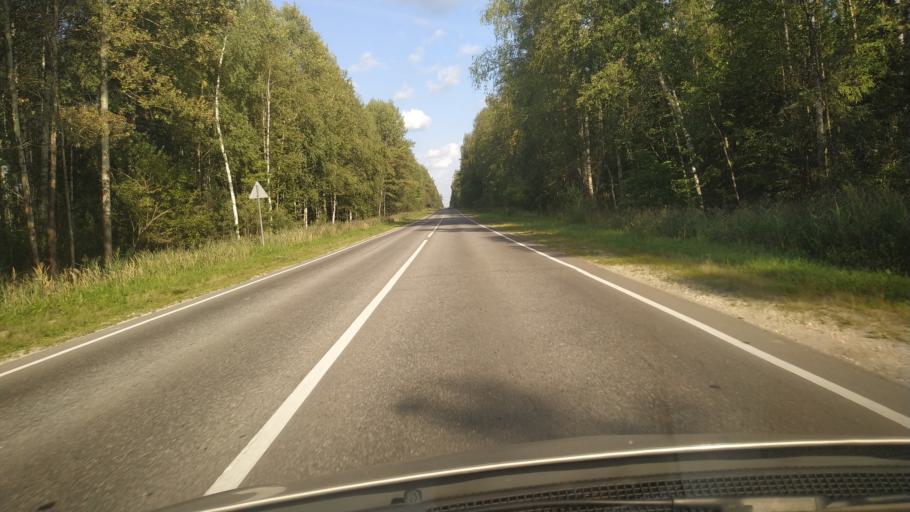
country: RU
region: Moskovskaya
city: Vereya
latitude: 55.7027
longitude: 39.1898
